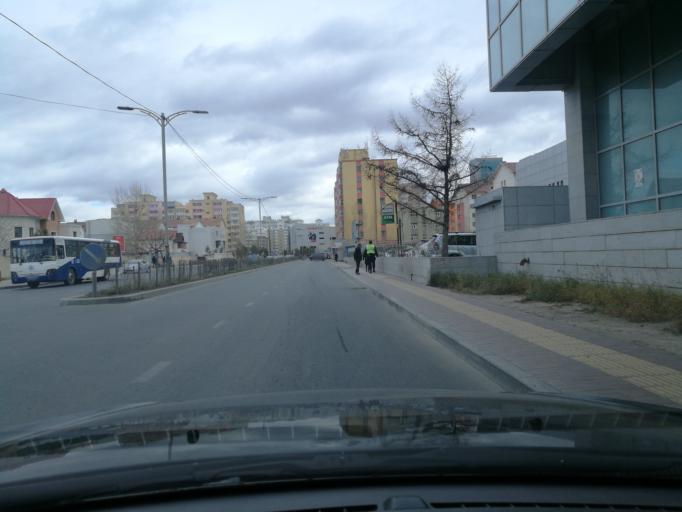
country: MN
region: Ulaanbaatar
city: Ulaanbaatar
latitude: 47.9044
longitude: 106.9225
